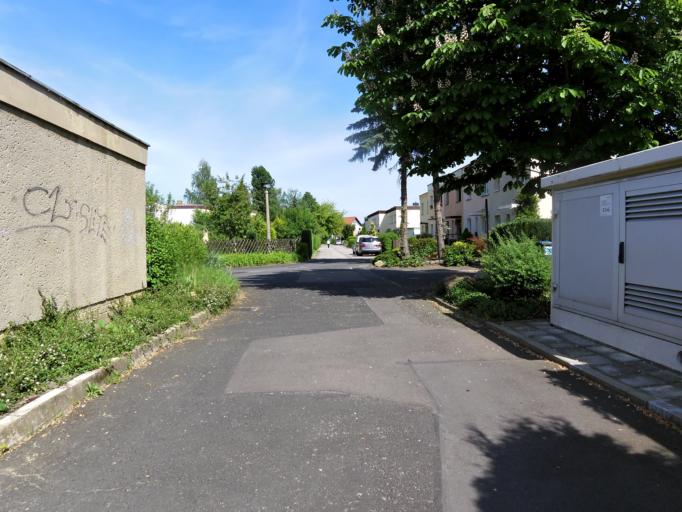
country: DE
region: Saxony
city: Leipzig
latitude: 51.3097
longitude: 12.4276
